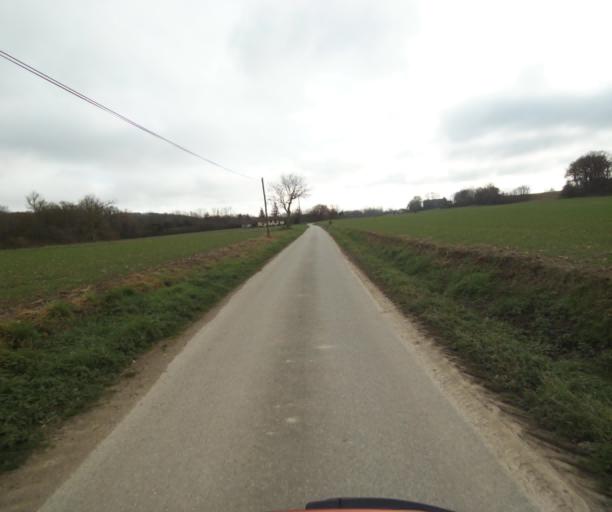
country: FR
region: Languedoc-Roussillon
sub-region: Departement de l'Aude
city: Belpech
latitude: 43.1821
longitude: 1.7343
